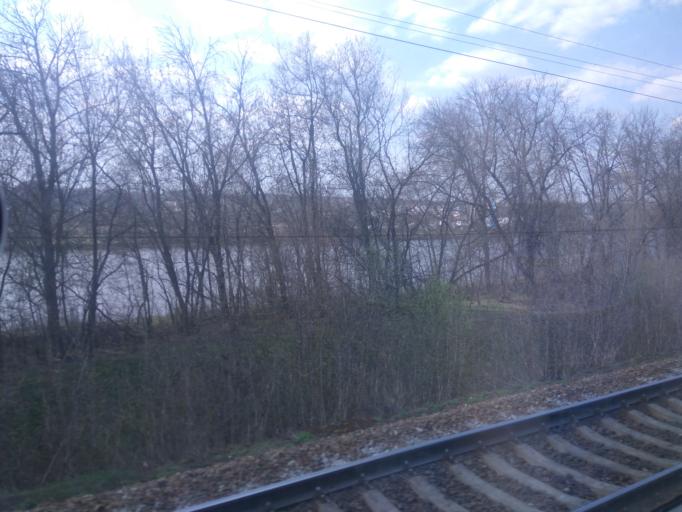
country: RU
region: Moskovskaya
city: Yakhroma
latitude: 56.2775
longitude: 37.5068
